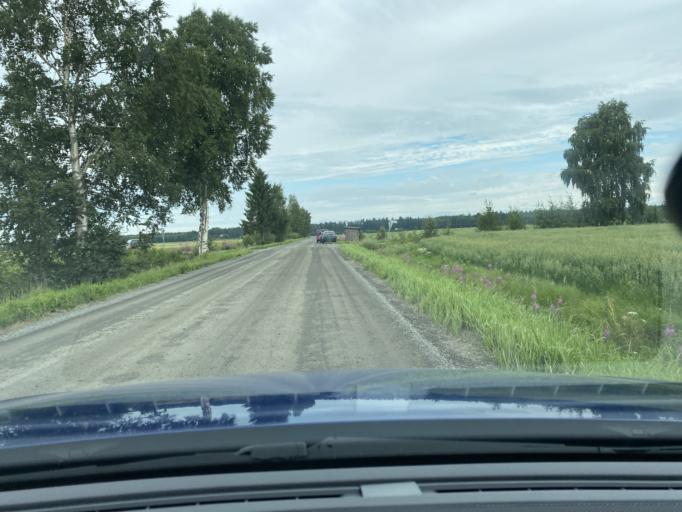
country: FI
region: Satakunta
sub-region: Rauma
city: Kiukainen
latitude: 61.1486
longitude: 22.0012
